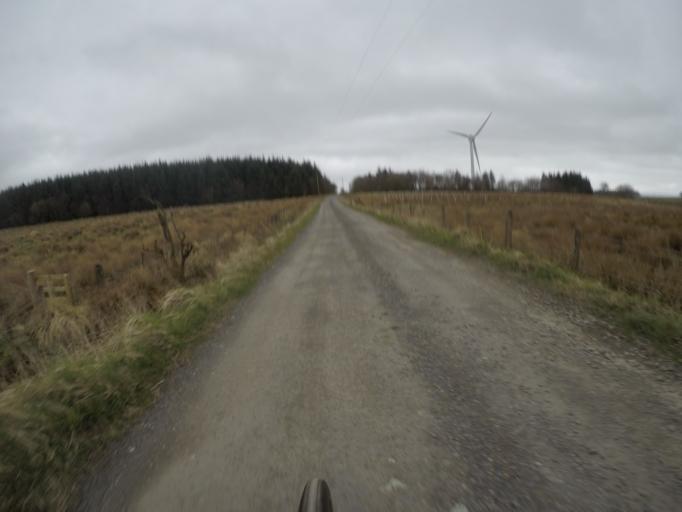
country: GB
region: Scotland
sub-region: East Ayrshire
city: Newmilns
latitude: 55.6287
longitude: -4.3423
